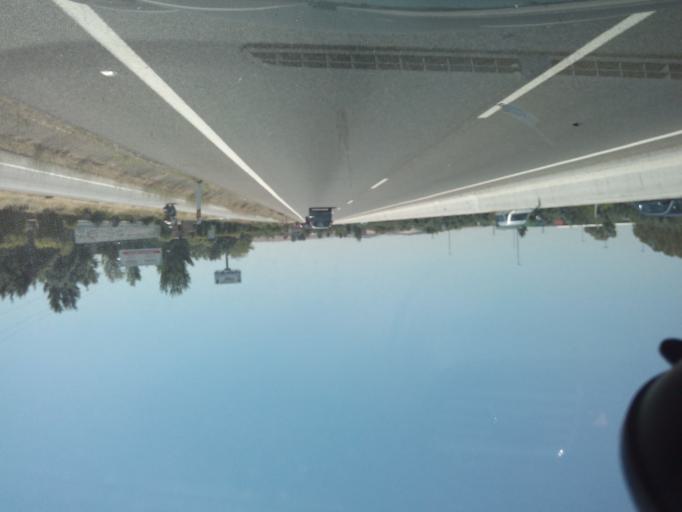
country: ES
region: Madrid
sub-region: Provincia de Madrid
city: San Sebastian de los Reyes
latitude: 40.5829
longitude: -3.5802
